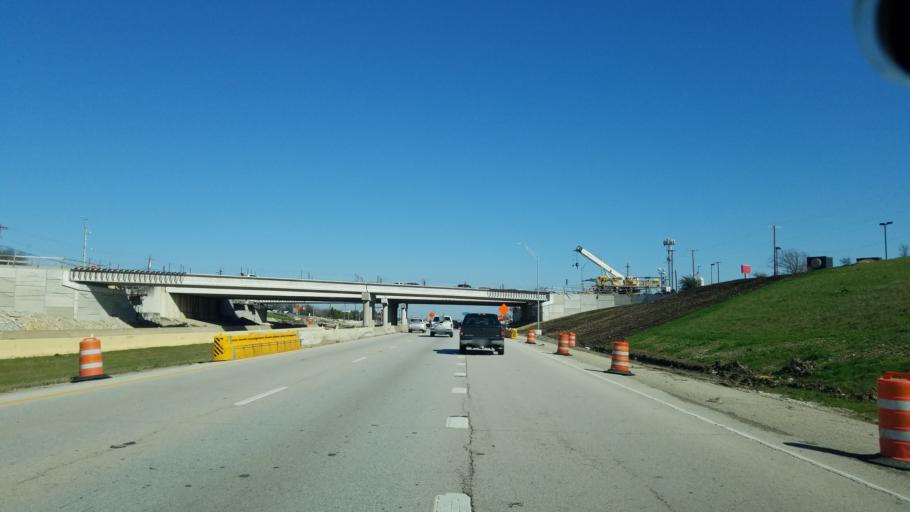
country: US
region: Texas
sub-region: Dallas County
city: Cedar Hill
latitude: 32.5888
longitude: -96.9471
